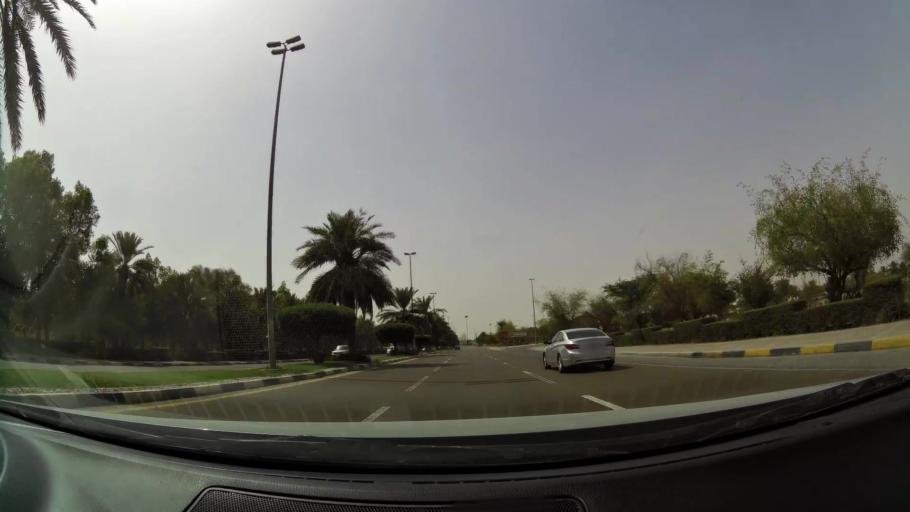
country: AE
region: Abu Dhabi
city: Al Ain
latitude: 24.1902
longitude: 55.6569
